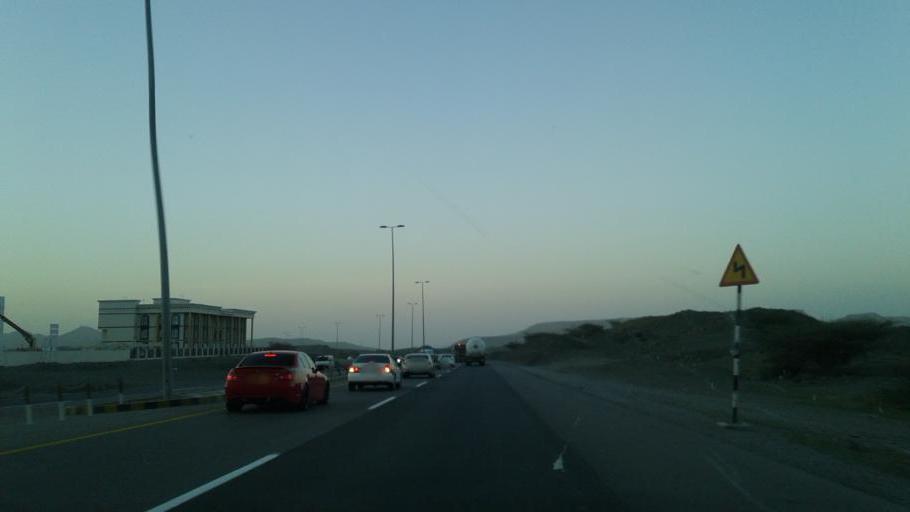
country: OM
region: Muhafazat ad Dakhiliyah
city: Bidbid
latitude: 23.4955
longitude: 58.1963
